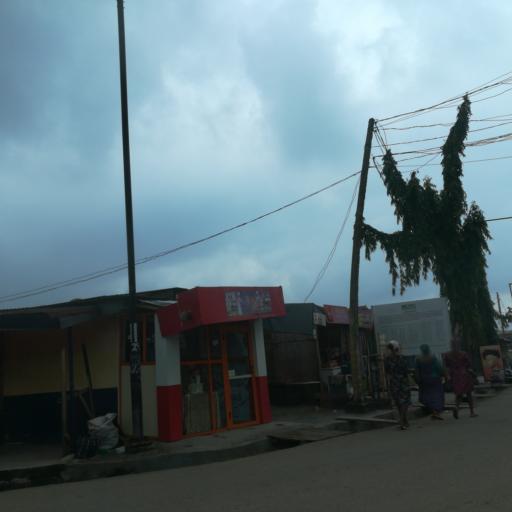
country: NG
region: Lagos
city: Agege
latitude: 6.6006
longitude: 3.3033
